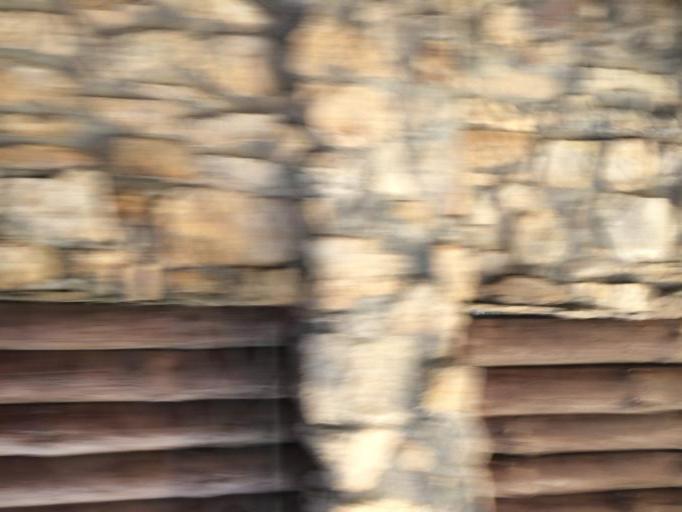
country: RU
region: Tula
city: Cherepet'
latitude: 54.1151
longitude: 36.3260
